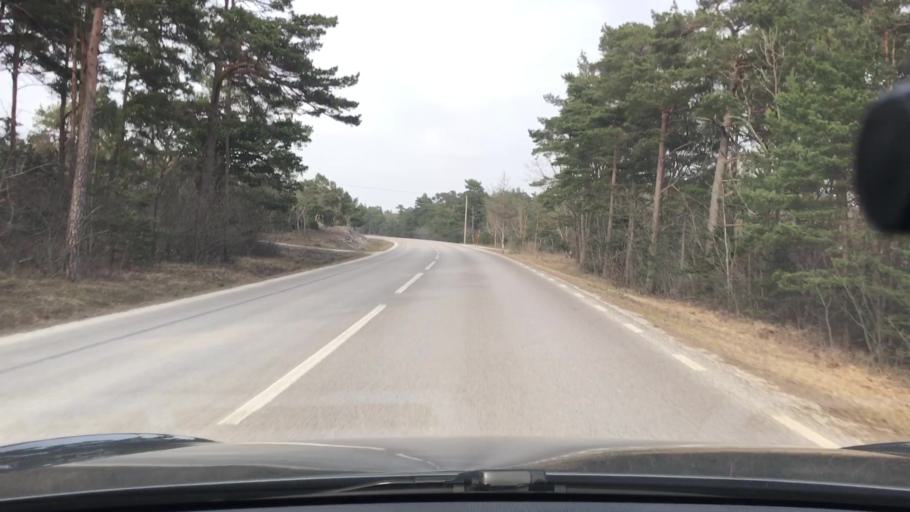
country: SE
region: Gotland
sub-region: Gotland
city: Slite
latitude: 57.4370
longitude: 18.6934
